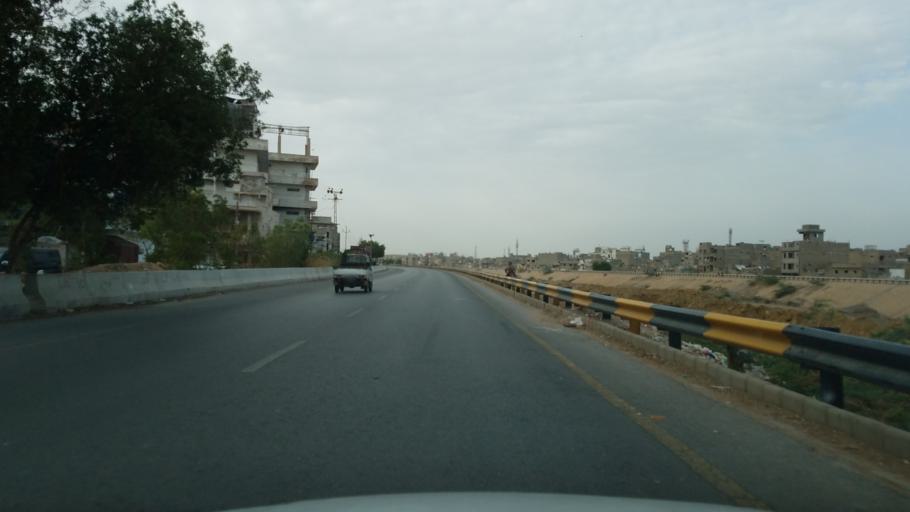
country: PK
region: Sindh
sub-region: Karachi District
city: Karachi
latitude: 24.9335
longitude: 67.0898
